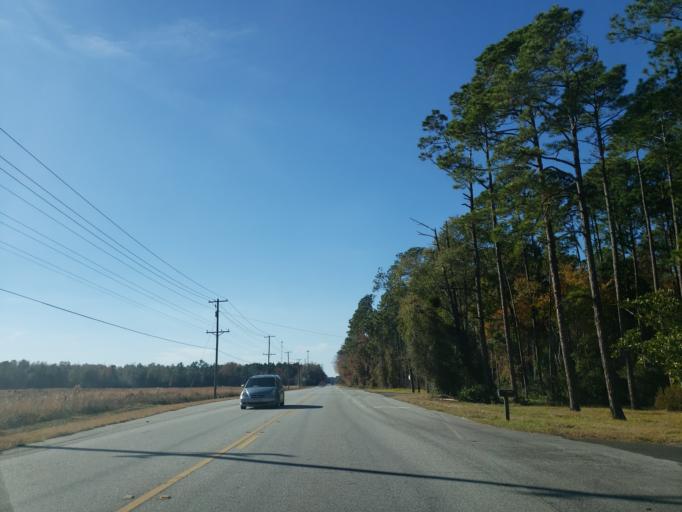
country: US
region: Georgia
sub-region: Glynn County
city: Dock Junction
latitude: 31.2725
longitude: -81.5405
